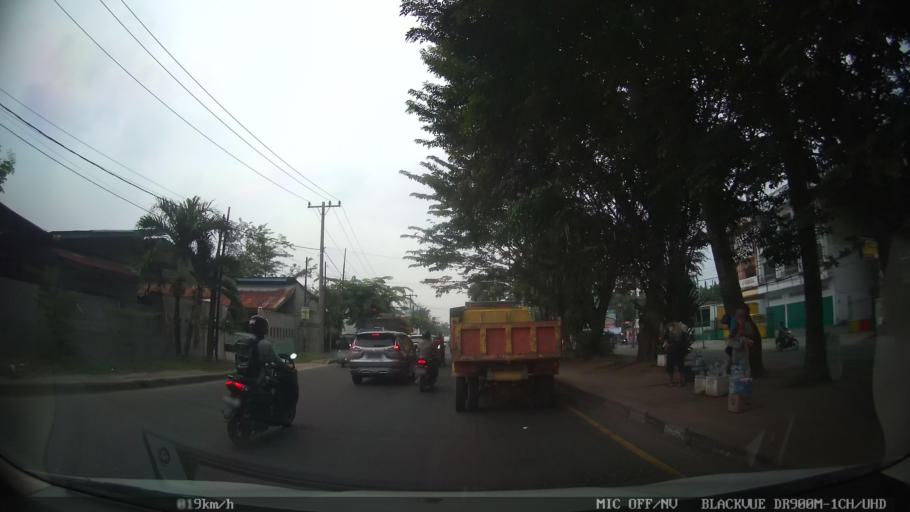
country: ID
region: North Sumatra
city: Deli Tua
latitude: 3.5381
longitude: 98.6907
